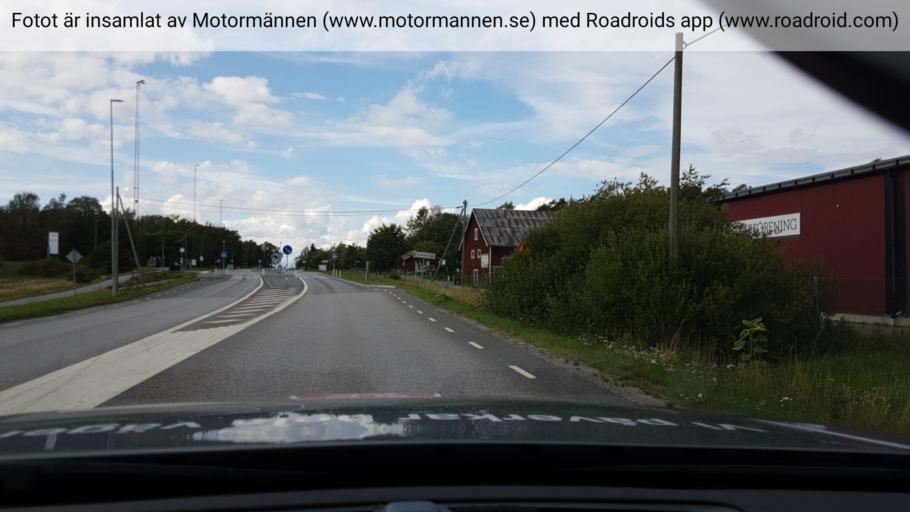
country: SE
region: Stockholm
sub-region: Upplands-Bro Kommun
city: Bro
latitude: 59.4938
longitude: 17.6837
